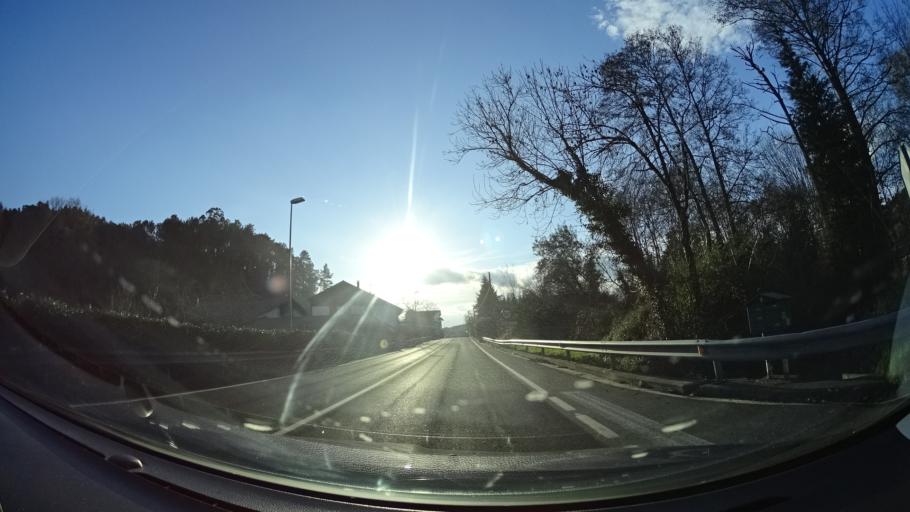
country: ES
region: Basque Country
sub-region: Bizkaia
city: Mungia
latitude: 43.3723
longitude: -2.8030
